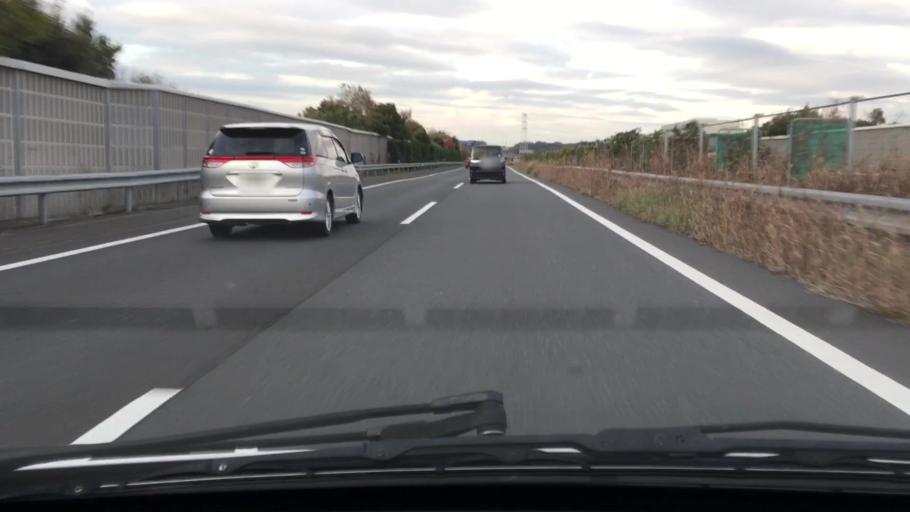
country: JP
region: Chiba
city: Kisarazu
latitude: 35.3992
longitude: 140.0060
